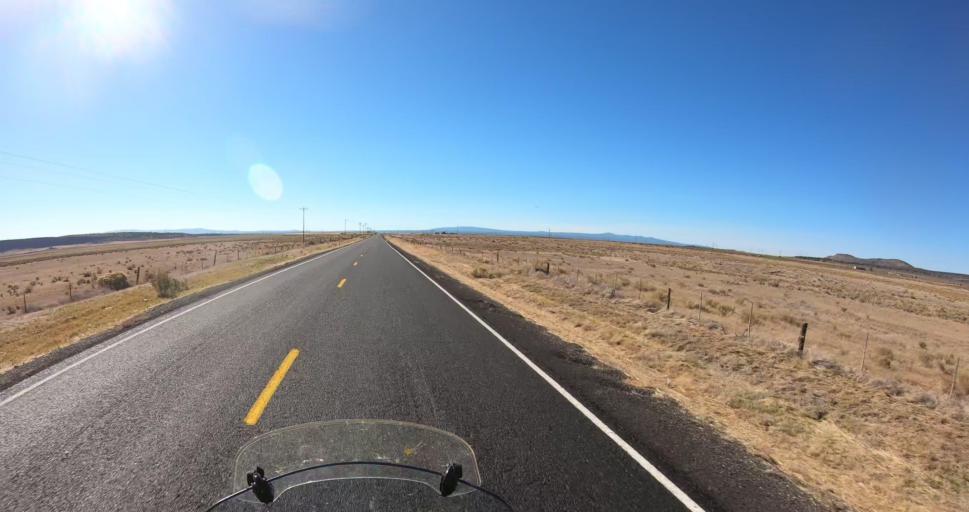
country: US
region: Oregon
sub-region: Deschutes County
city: La Pine
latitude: 43.1307
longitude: -120.9146
